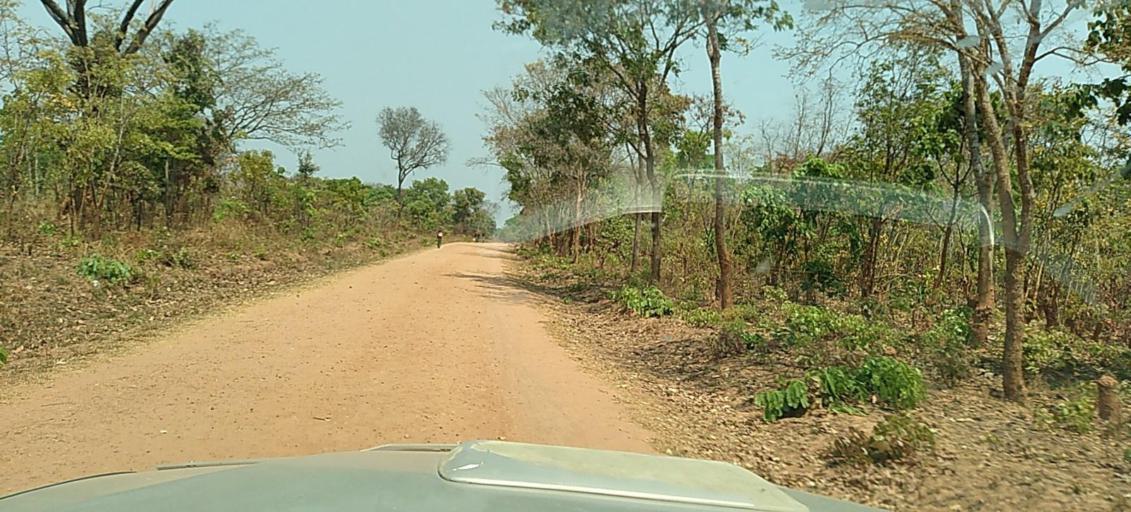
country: ZM
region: North-Western
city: Kasempa
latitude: -13.6999
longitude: 26.3303
